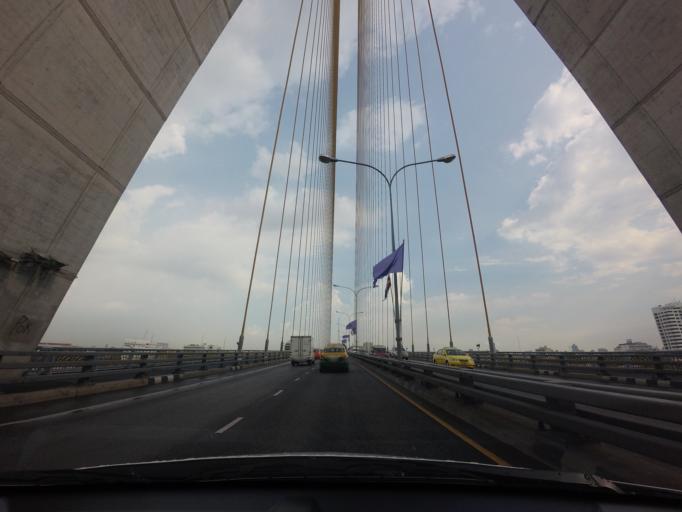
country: TH
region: Bangkok
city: Phra Nakhon
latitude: 13.7698
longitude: 100.4959
